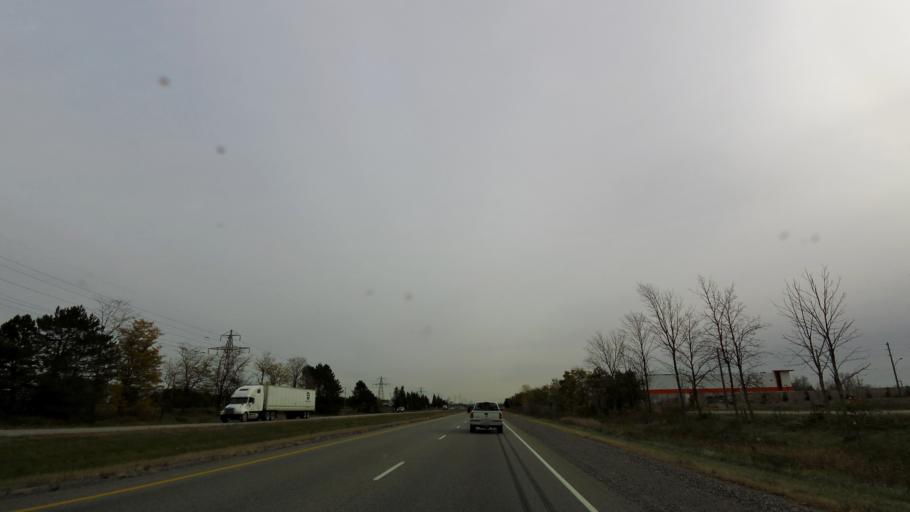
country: CA
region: Ontario
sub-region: Wellington County
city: Guelph
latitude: 43.4977
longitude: -80.2232
